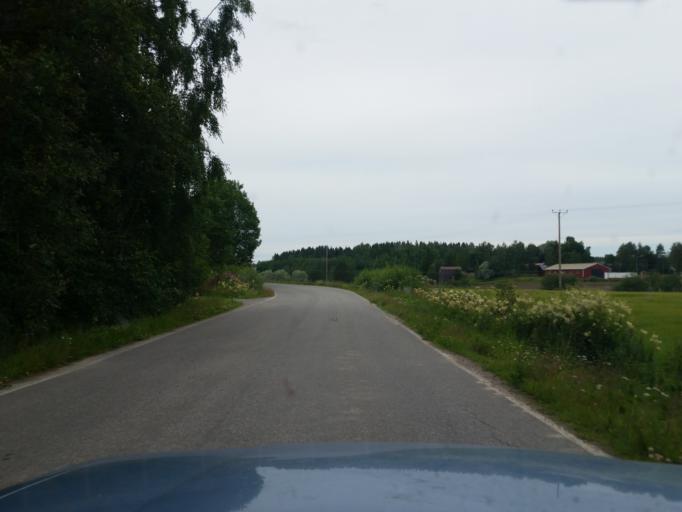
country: FI
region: Uusimaa
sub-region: Helsinki
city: Sammatti
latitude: 60.4722
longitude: 23.8261
